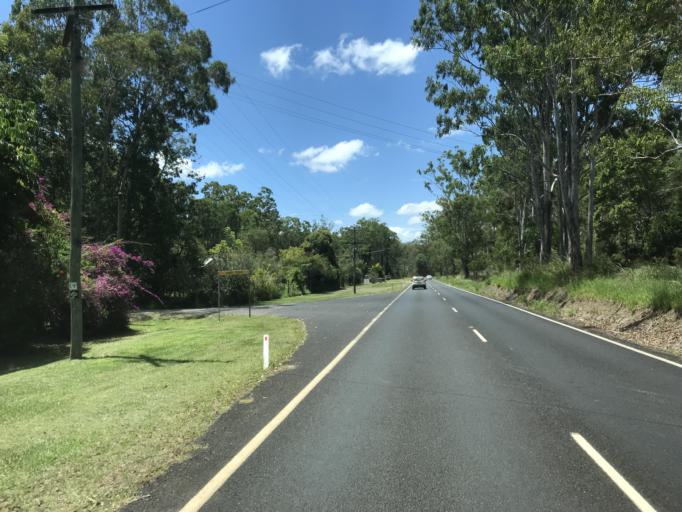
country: AU
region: Queensland
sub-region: Tablelands
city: Atherton
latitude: -17.4086
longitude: 145.3909
